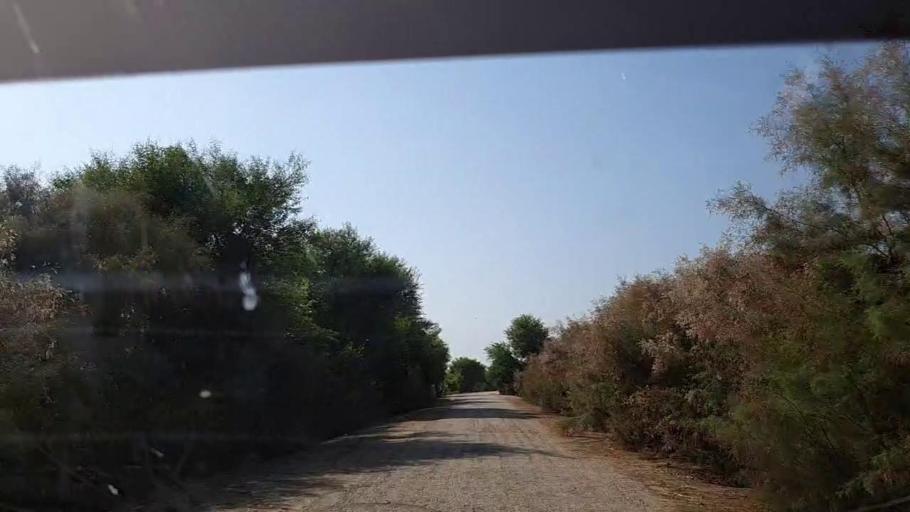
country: PK
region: Sindh
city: Ghauspur
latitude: 28.1900
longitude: 69.0586
